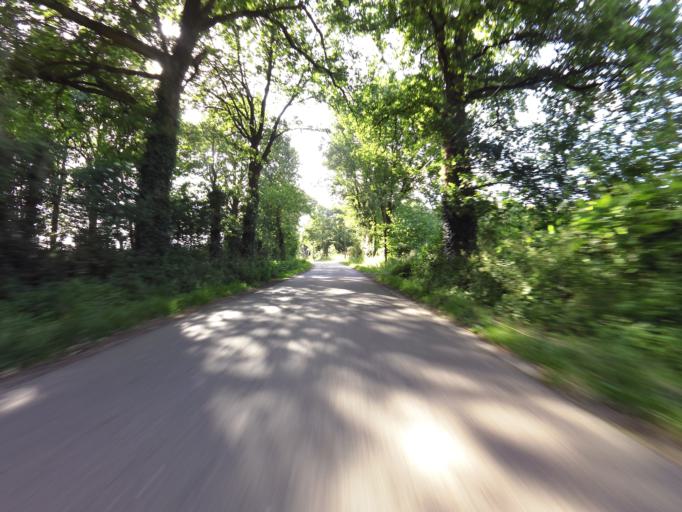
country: FR
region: Brittany
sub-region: Departement du Morbihan
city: Pluherlin
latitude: 47.7036
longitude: -2.3863
